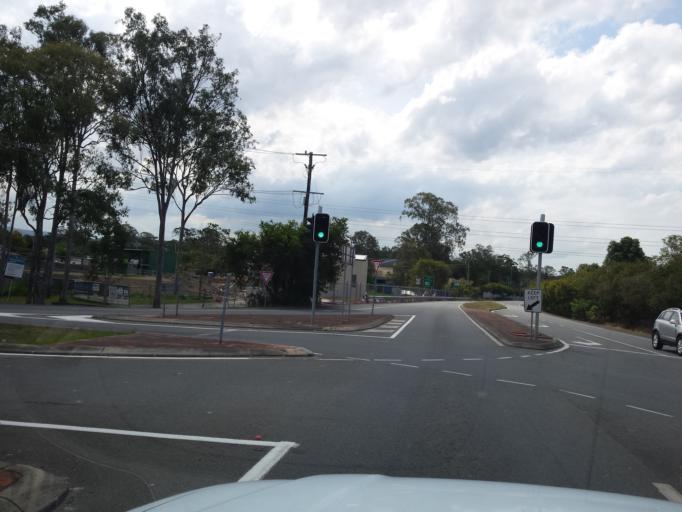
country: AU
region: Queensland
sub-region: Gold Coast
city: Nerang
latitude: -28.0060
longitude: 153.3411
